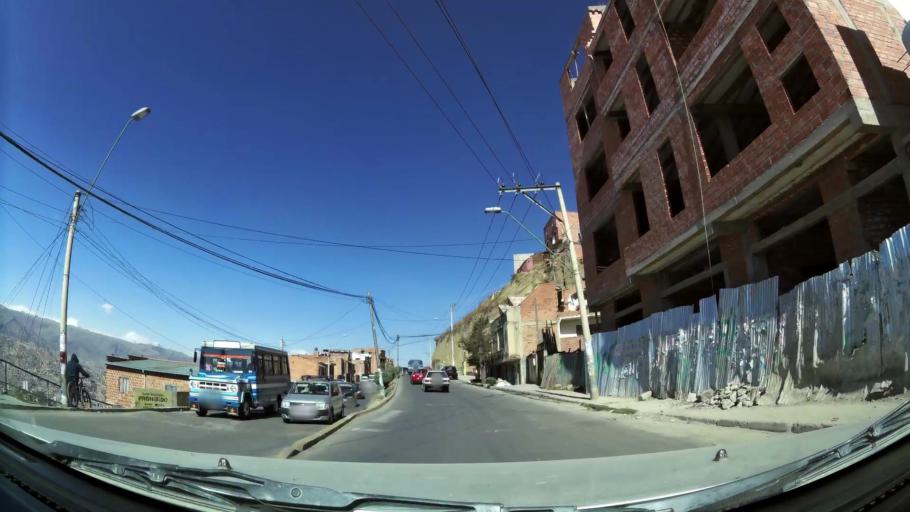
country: BO
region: La Paz
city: La Paz
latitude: -16.5178
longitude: -68.1417
